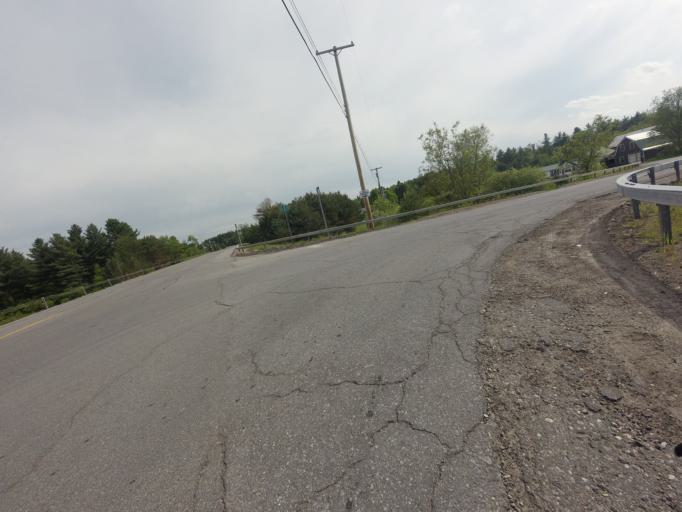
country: US
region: New York
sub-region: St. Lawrence County
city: Gouverneur
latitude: 44.2812
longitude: -75.2048
